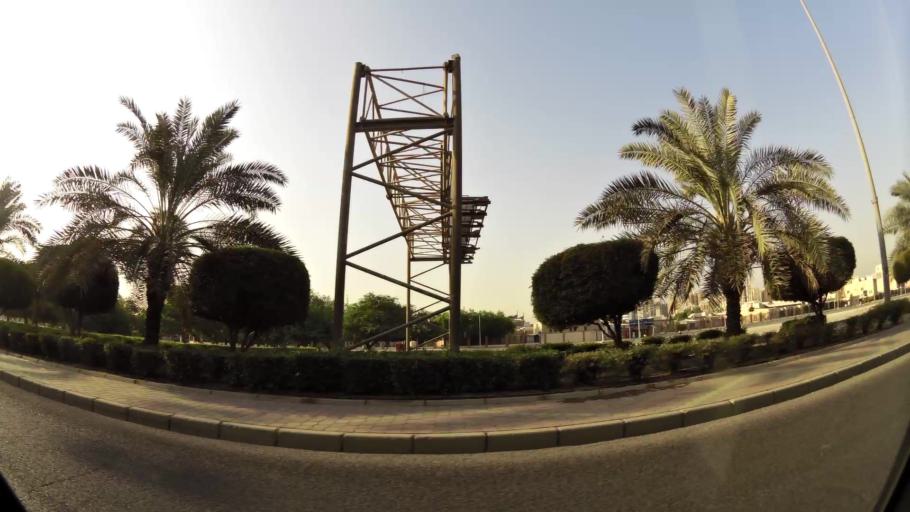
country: KW
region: Muhafazat Hawalli
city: Hawalli
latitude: 29.3452
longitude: 48.0278
